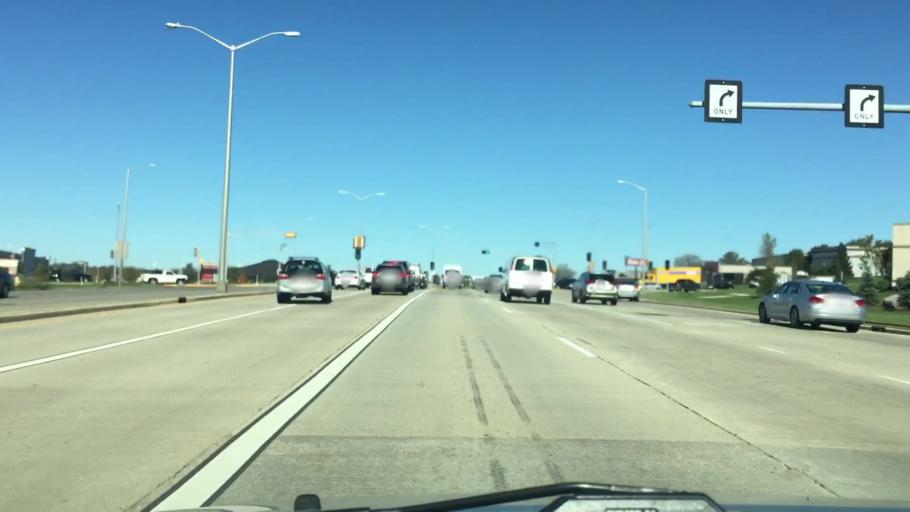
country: US
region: Wisconsin
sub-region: Waukesha County
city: Waukesha
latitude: 43.0198
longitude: -88.2011
